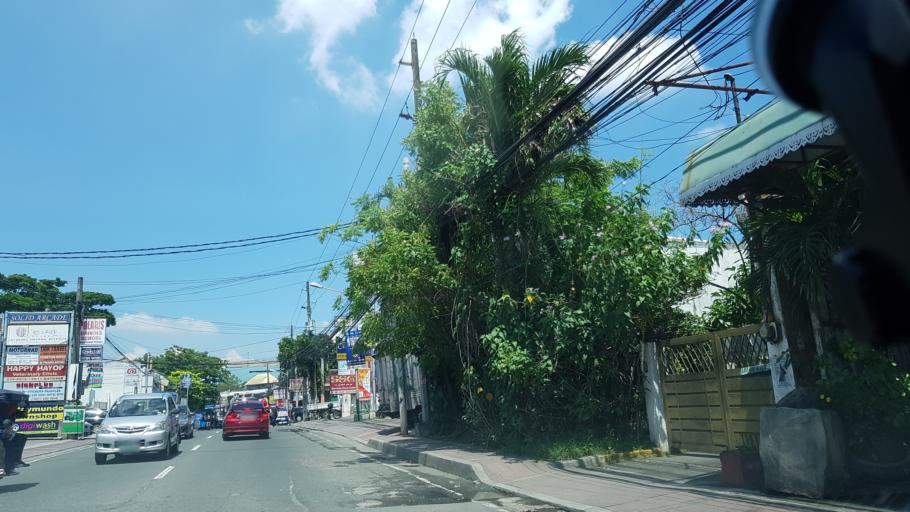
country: PH
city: Sambayanihan People's Village
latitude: 14.4541
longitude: 121.0305
